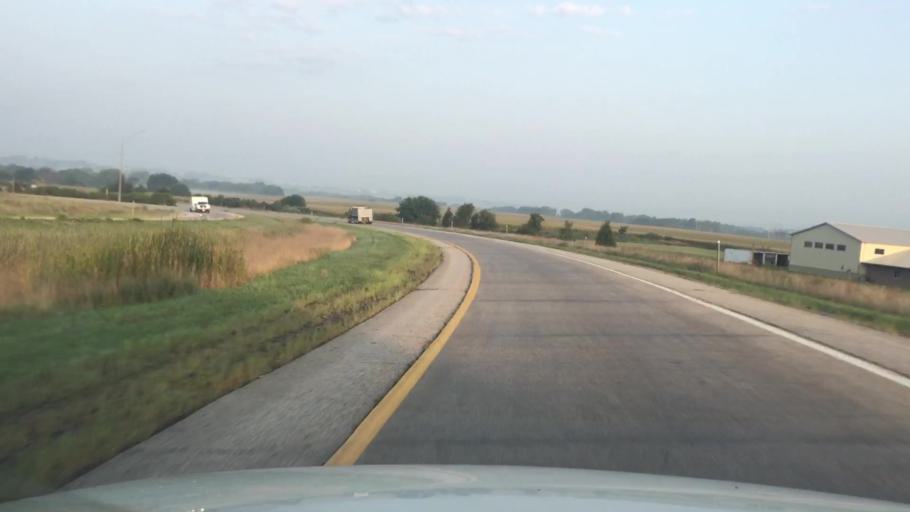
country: US
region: Iowa
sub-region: Polk County
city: Altoona
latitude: 41.6611
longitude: -93.5235
